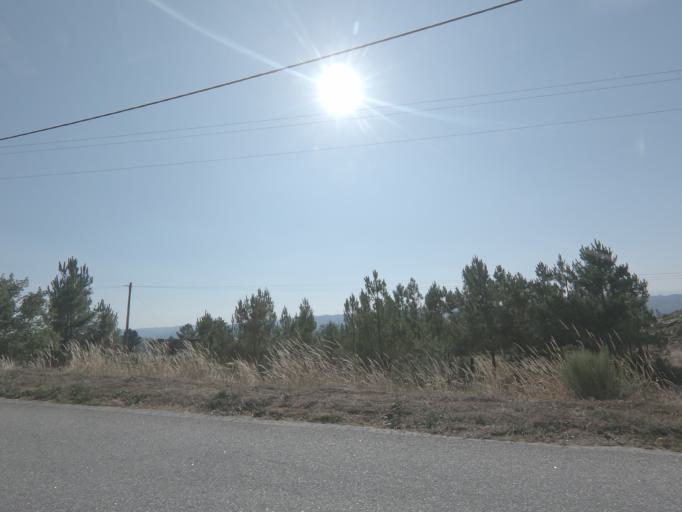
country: PT
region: Viseu
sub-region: Tabuaco
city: Tabuaco
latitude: 41.0436
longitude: -7.5712
